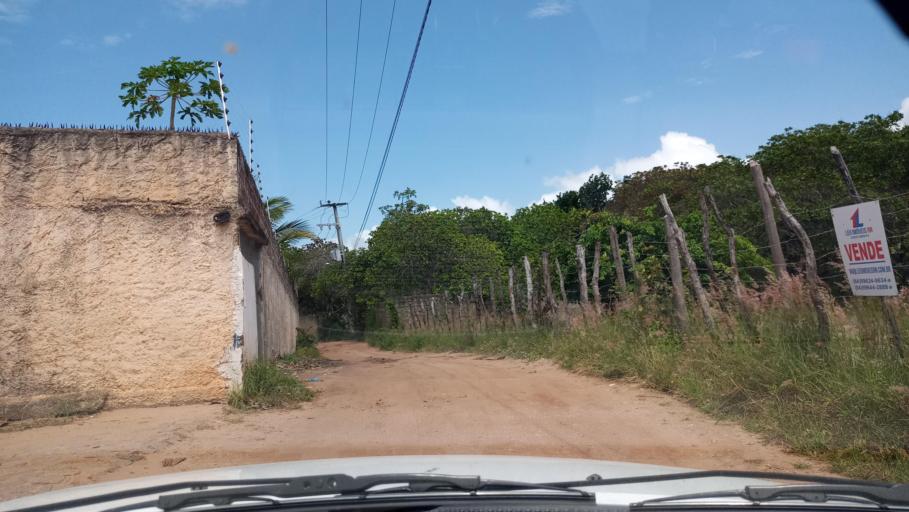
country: BR
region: Rio Grande do Norte
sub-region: Ares
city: Ares
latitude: -6.2405
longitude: -35.0451
